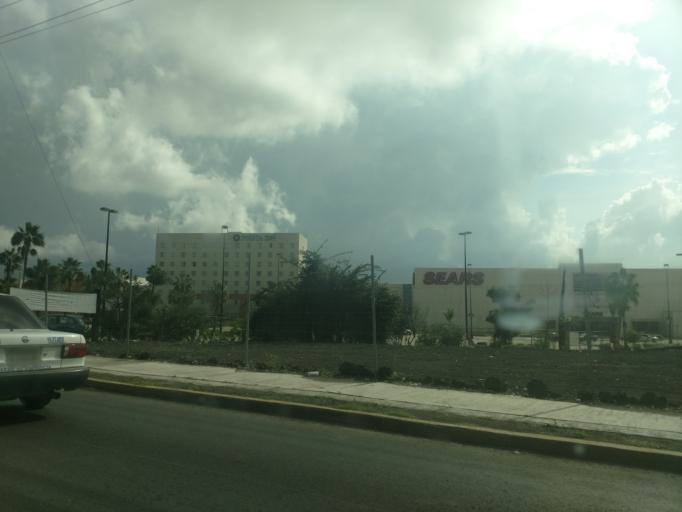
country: MX
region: Nayarit
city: Tepic
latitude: 21.4938
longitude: -104.8667
